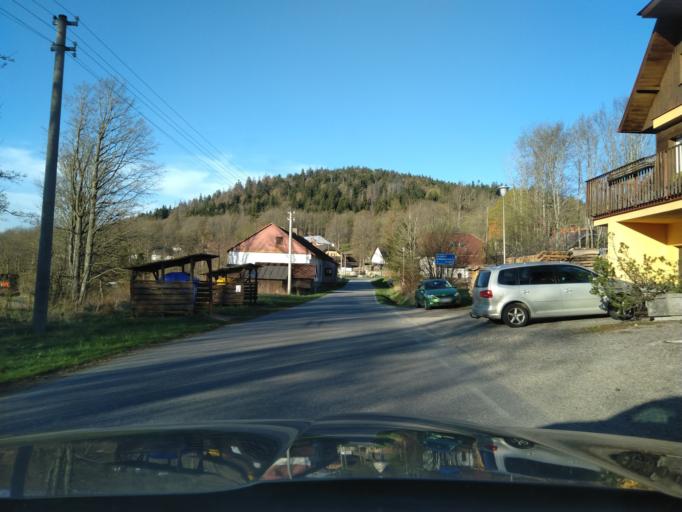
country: DE
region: Bavaria
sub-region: Lower Bavaria
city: Haidmuhle
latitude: 48.8799
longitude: 13.7774
